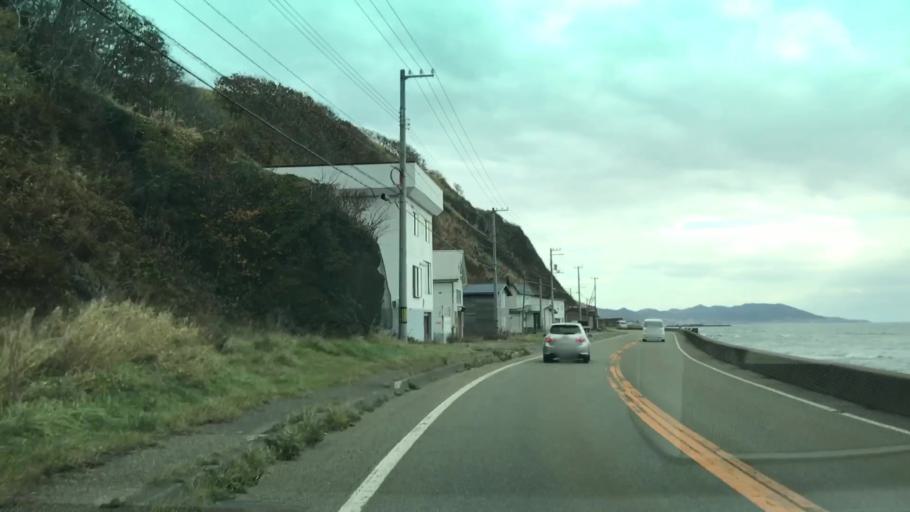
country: JP
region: Hokkaido
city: Shizunai-furukawacho
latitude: 42.0554
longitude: 143.0824
